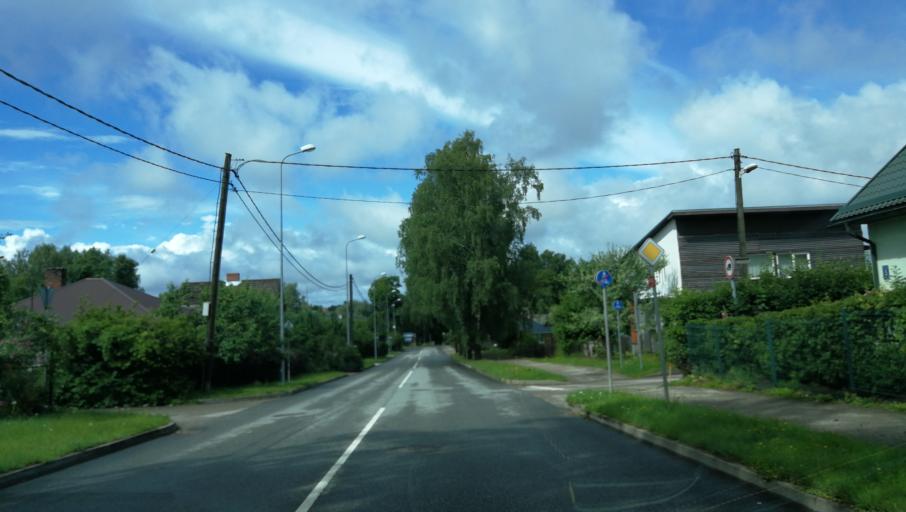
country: LV
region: Cesu Rajons
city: Cesis
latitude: 57.3064
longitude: 25.2415
